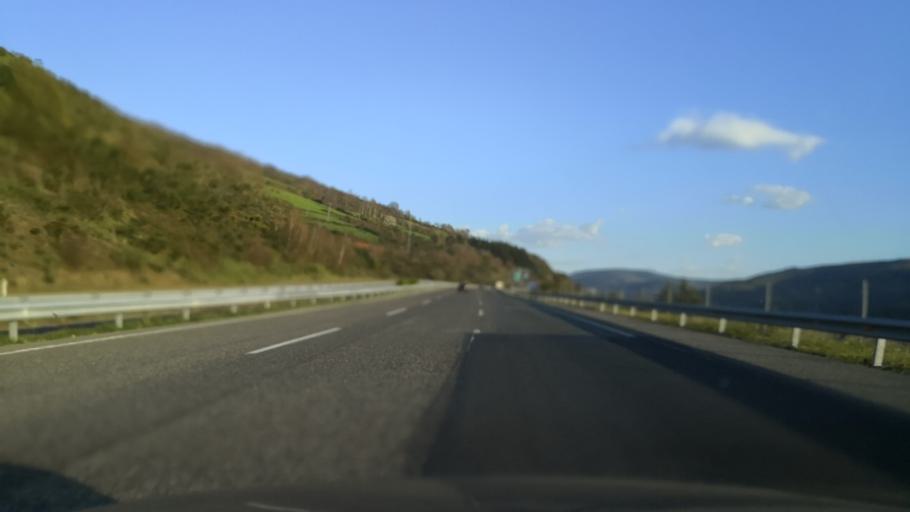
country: ES
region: Galicia
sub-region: Provincia de Lugo
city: San Roman
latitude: 42.7732
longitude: -7.0940
